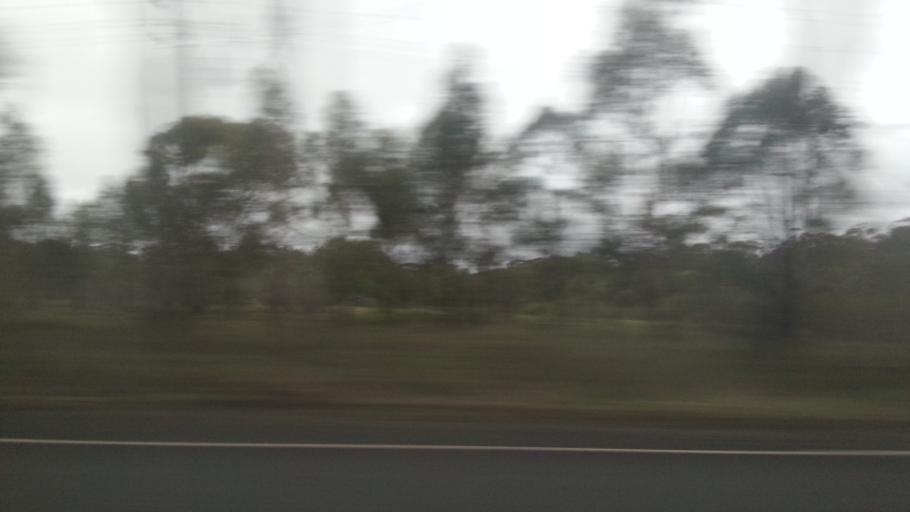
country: AU
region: New South Wales
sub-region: Wollondilly
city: Douglas Park
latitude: -34.2168
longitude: 150.7232
